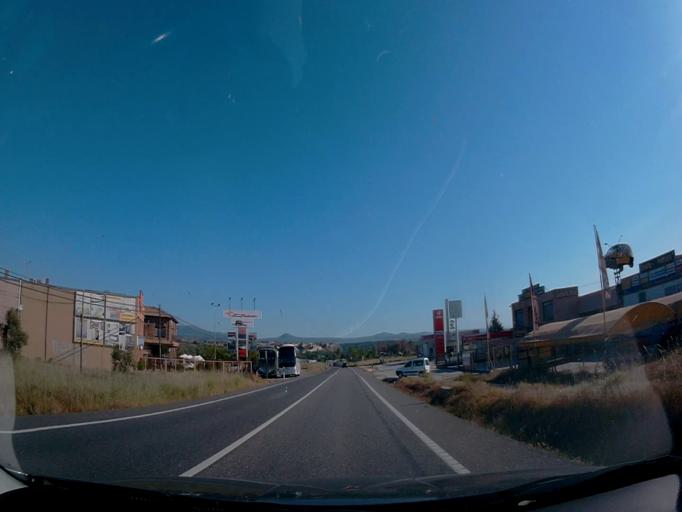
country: ES
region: Castille-La Mancha
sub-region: Province of Toledo
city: Escalona
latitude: 40.1477
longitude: -4.4026
